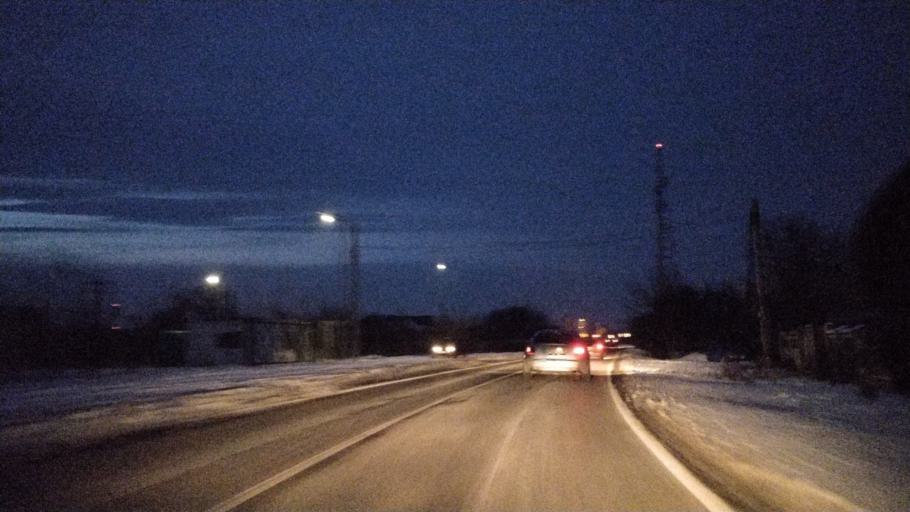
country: RO
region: Vrancea
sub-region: Comuna Milcovul
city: Milcovul
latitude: 45.6782
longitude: 27.2365
